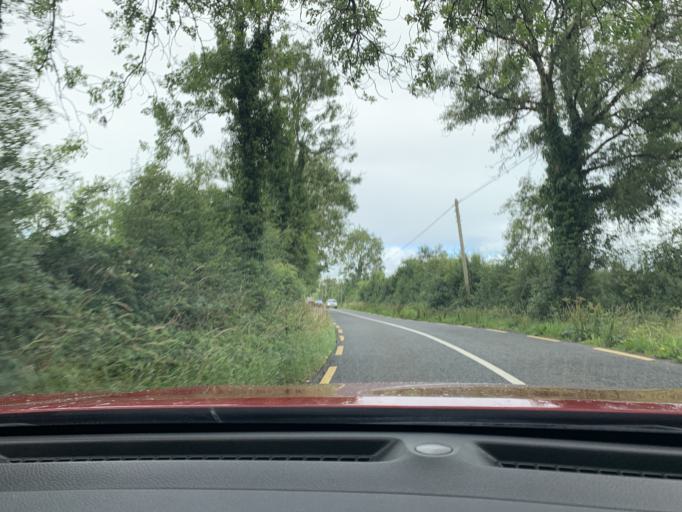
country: IE
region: Connaught
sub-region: County Leitrim
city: Carrick-on-Shannon
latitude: 53.8739
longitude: -8.1512
